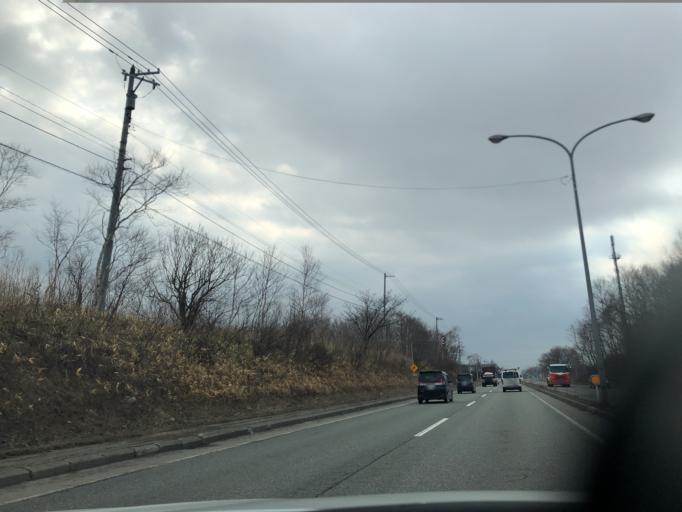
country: JP
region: Hokkaido
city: Chitose
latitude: 42.7774
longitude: 141.7043
